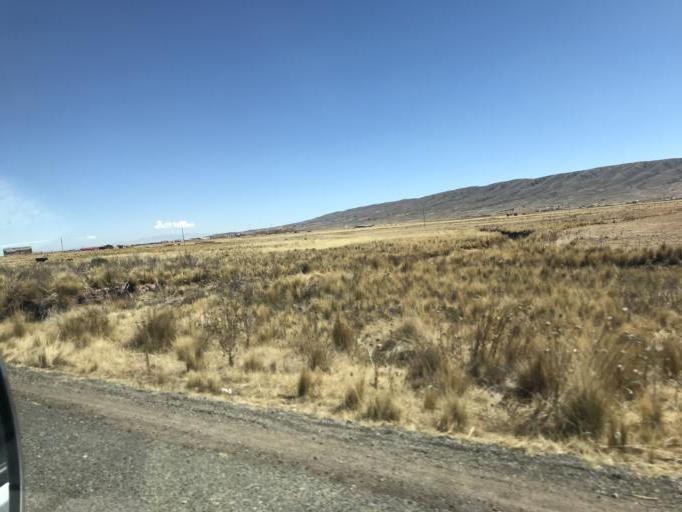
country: BO
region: La Paz
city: Tiahuanaco
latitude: -16.5680
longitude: -68.6553
